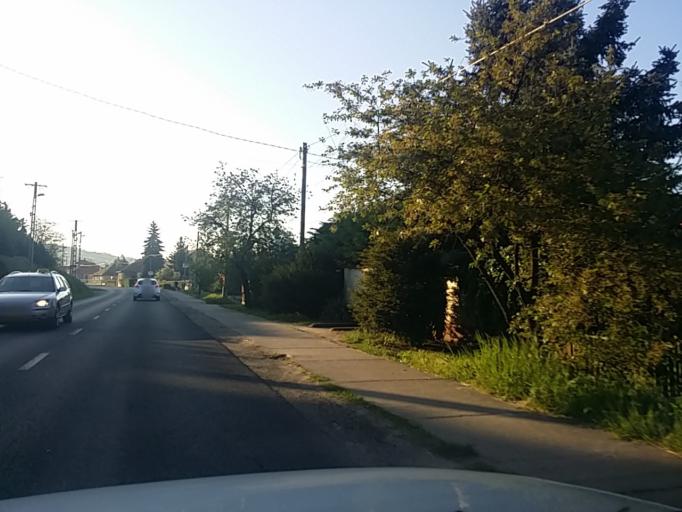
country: HU
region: Pest
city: Mogyorod
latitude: 47.5965
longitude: 19.2307
